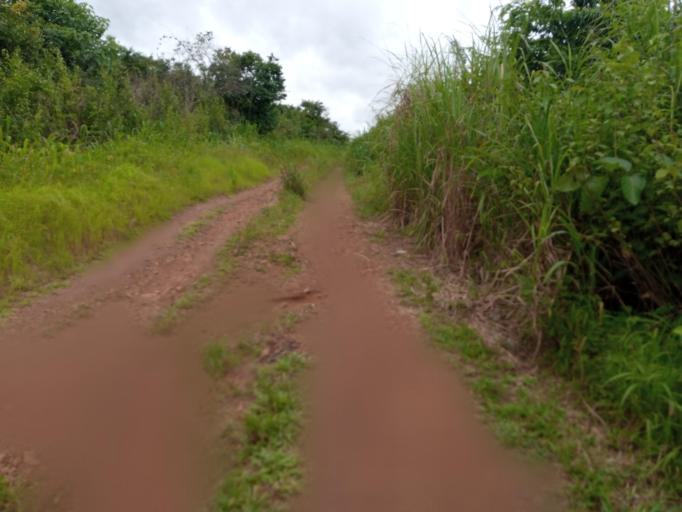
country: SL
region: Southern Province
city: Largo
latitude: 8.1990
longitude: -12.0517
